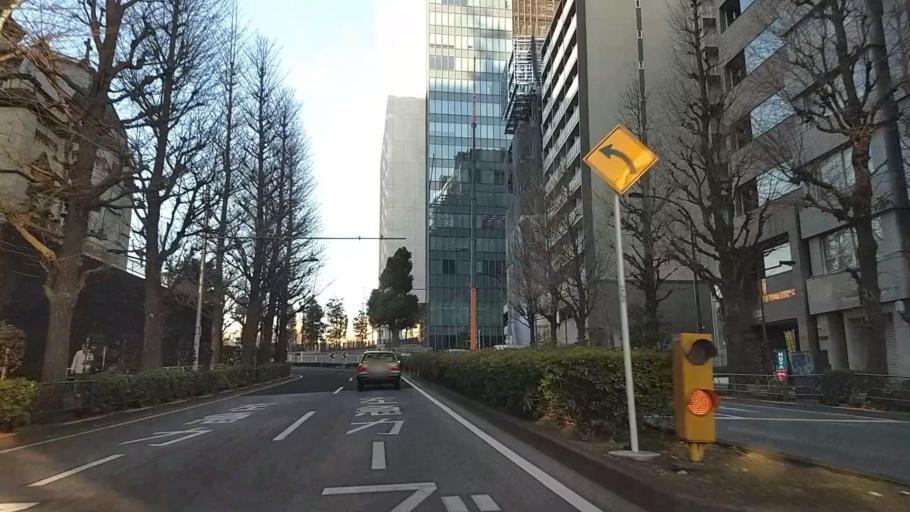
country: JP
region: Tokyo
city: Tokyo
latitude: 35.6974
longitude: 139.7658
